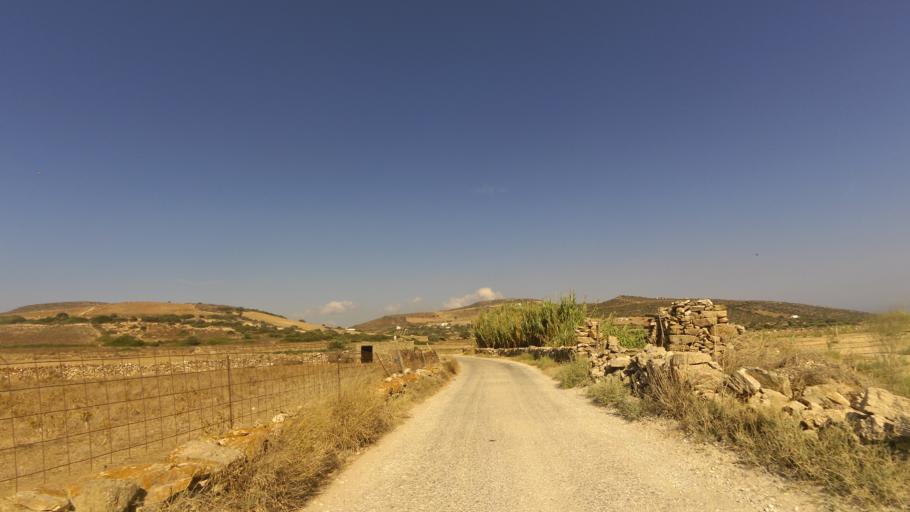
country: GR
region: South Aegean
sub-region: Nomos Kykladon
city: Antiparos
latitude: 37.0169
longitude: 25.0543
